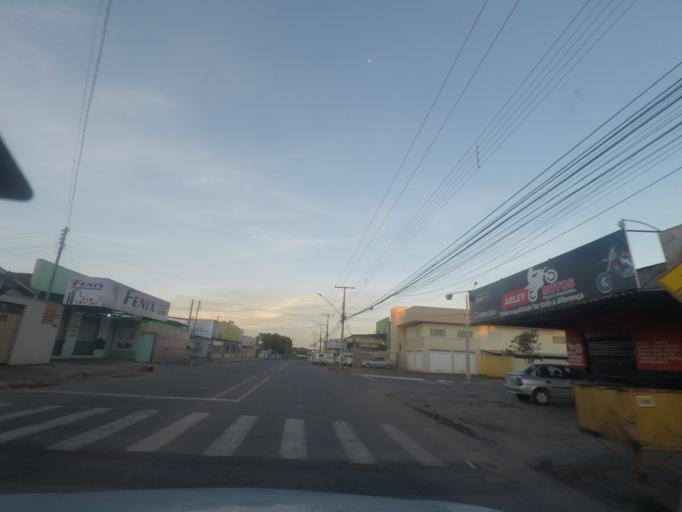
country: BR
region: Goias
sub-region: Goiania
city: Goiania
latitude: -16.6893
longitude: -49.3367
